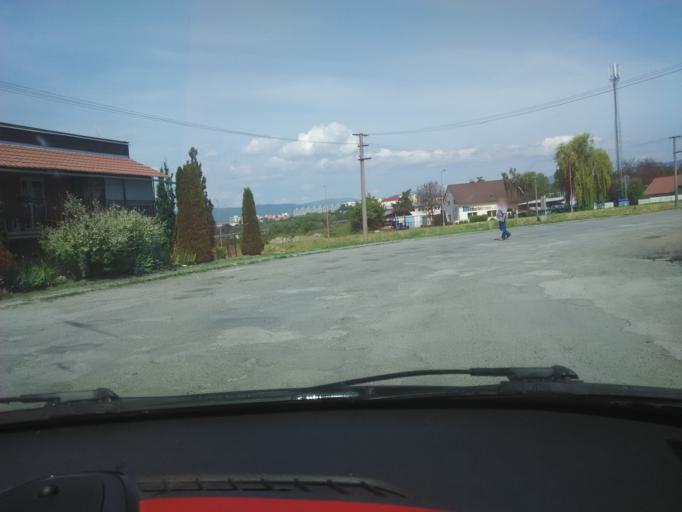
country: SK
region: Banskobystricky
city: Ziar nad Hronom
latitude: 48.5785
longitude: 18.8693
